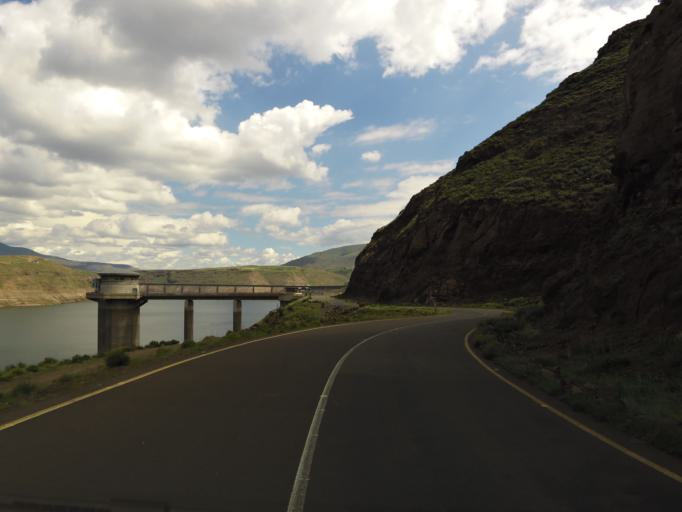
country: LS
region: Thaba-Tseka
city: Thaba-Tseka
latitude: -29.1699
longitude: 28.4826
